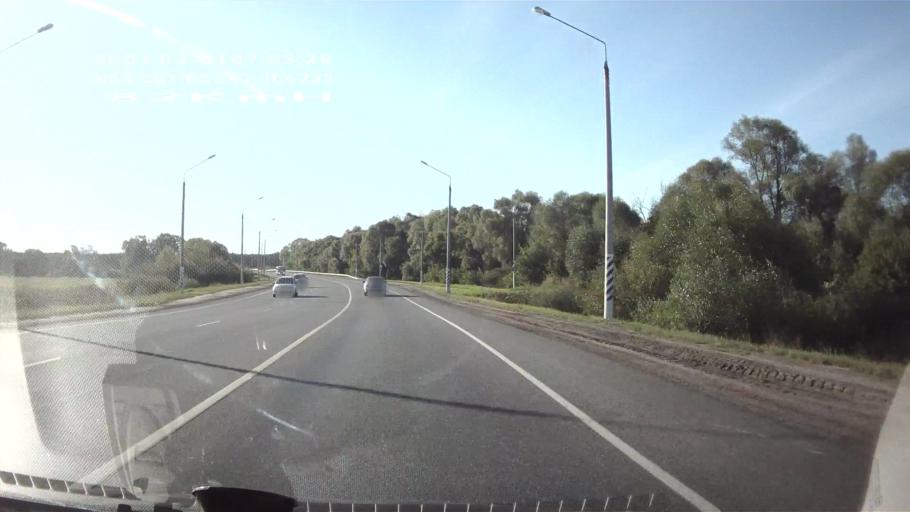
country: RU
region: Chuvashia
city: Shikhazany
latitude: 55.5609
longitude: 47.4045
